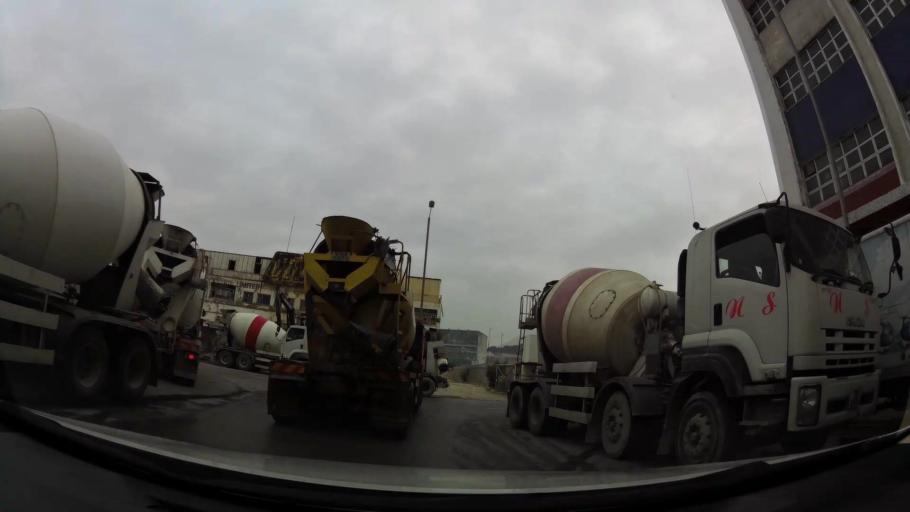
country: HK
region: Kowloon City
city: Kowloon
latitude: 22.2947
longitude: 114.2336
